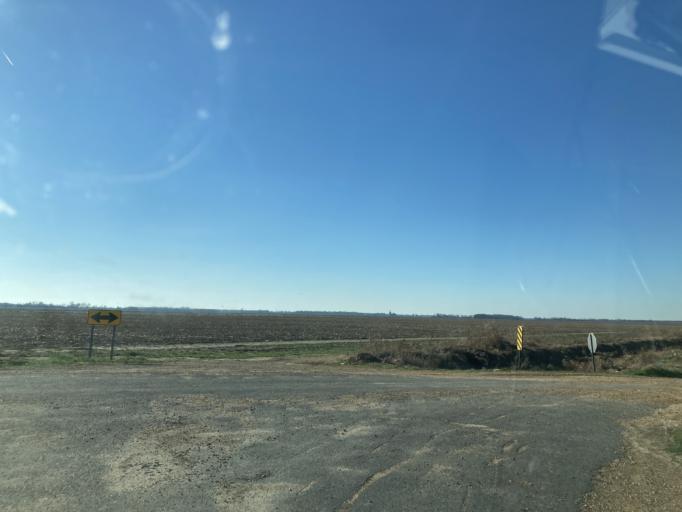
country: US
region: Mississippi
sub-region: Yazoo County
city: Yazoo City
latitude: 32.9520
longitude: -90.6056
